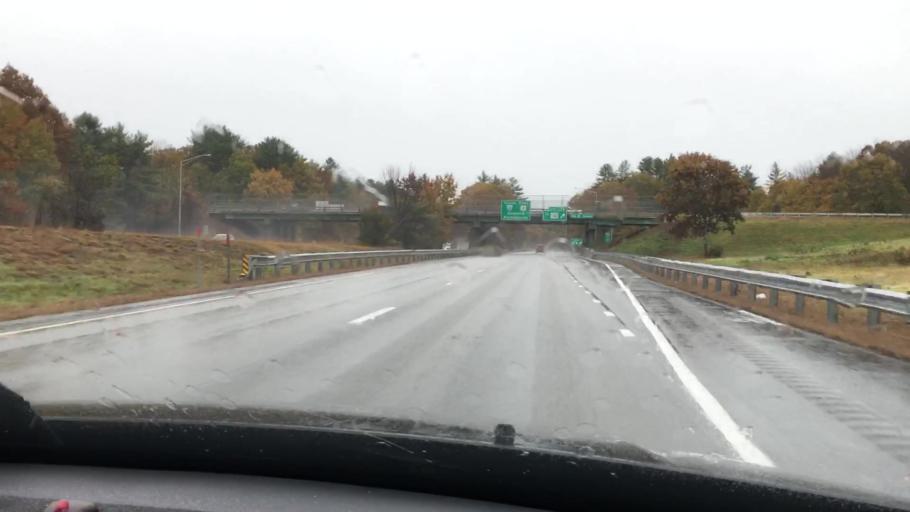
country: US
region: New Hampshire
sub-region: Merrimack County
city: Canterbury
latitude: 43.2927
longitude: -71.5741
